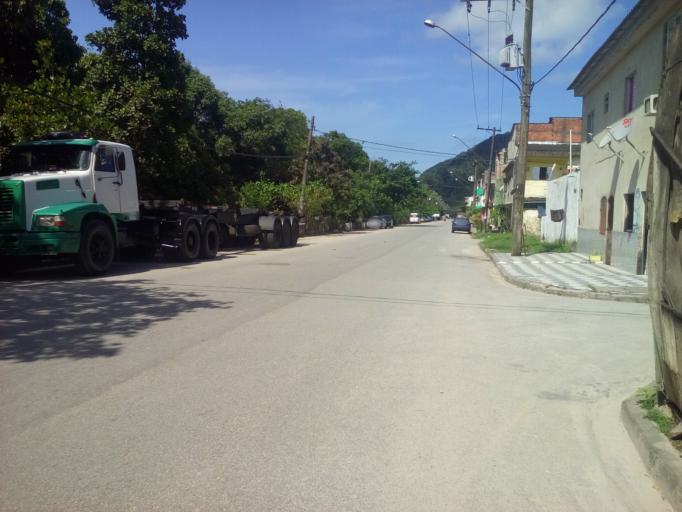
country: BR
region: Sao Paulo
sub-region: Guaruja
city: Guaruja
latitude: -23.9592
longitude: -46.2502
